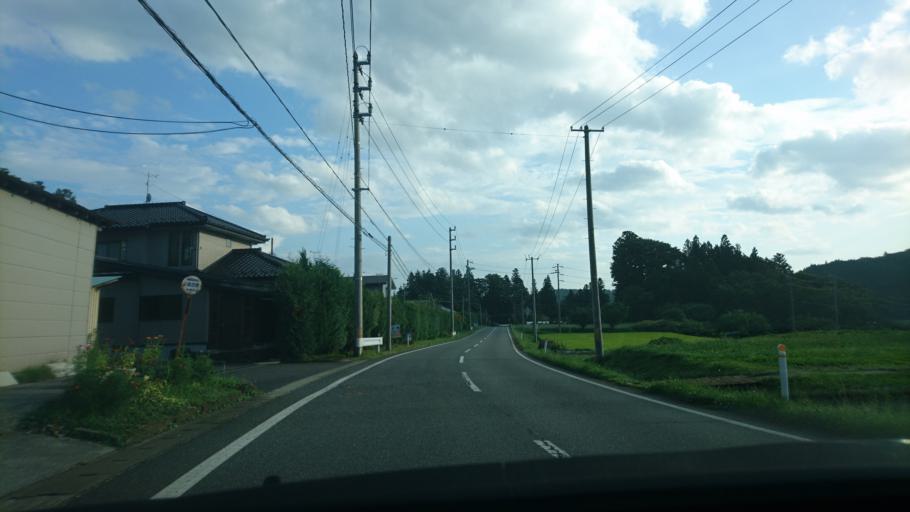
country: JP
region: Iwate
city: Mizusawa
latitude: 39.0284
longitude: 141.2946
